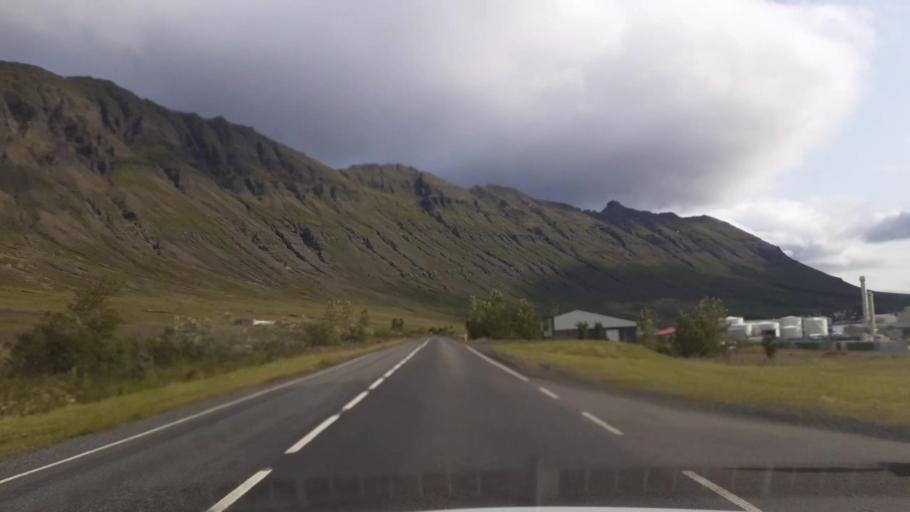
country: IS
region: East
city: Neskaupstadur
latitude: 65.1379
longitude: -13.7457
